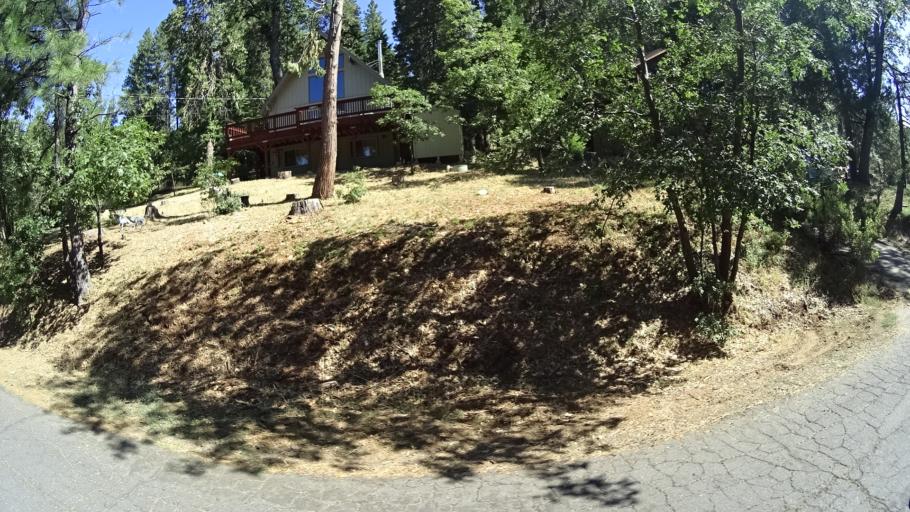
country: US
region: California
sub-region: Calaveras County
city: Arnold
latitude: 38.2495
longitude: -120.3706
